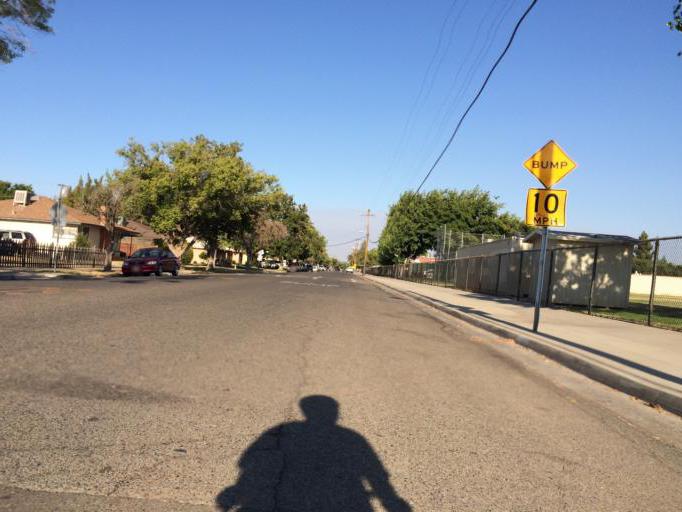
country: US
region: California
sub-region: Fresno County
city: Fresno
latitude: 36.7759
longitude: -119.7601
